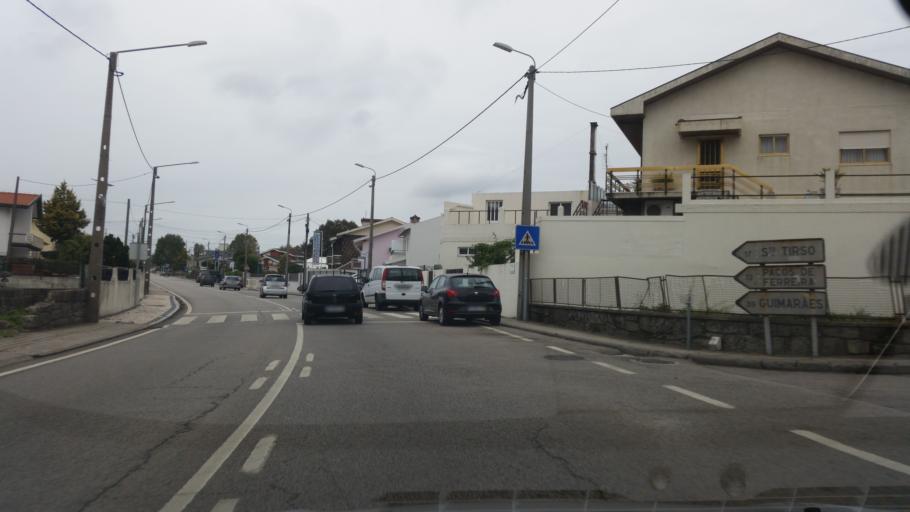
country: PT
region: Porto
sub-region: Valongo
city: Ermesinde
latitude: 41.2260
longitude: -8.5540
